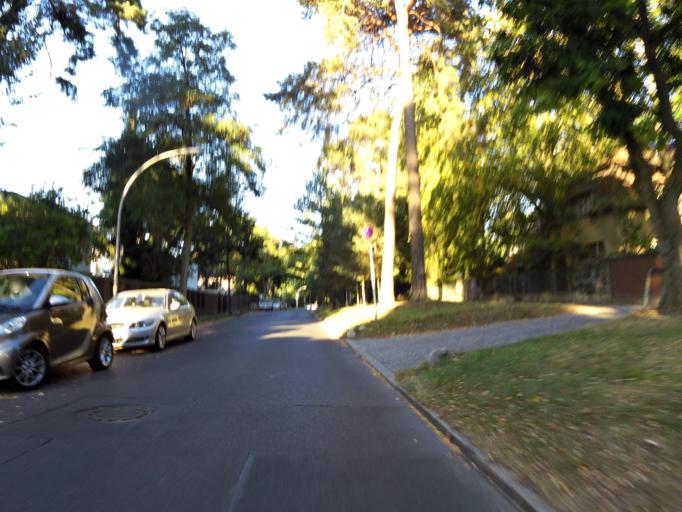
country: DE
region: Berlin
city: Dahlem
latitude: 52.4644
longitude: 13.2847
